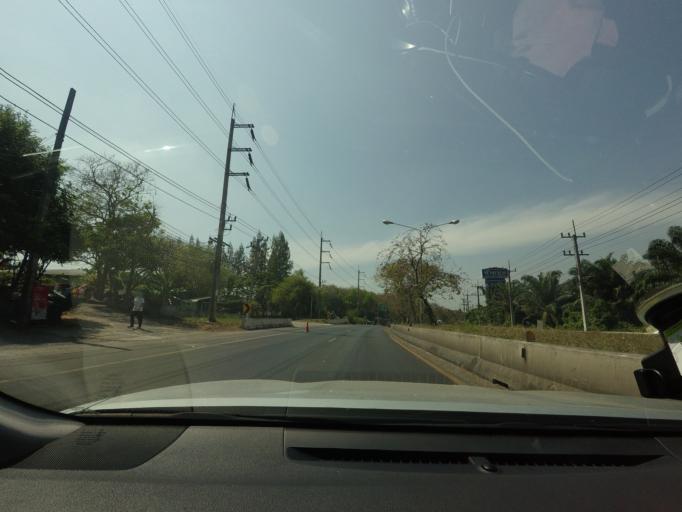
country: TH
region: Surat Thani
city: Kanchanadit
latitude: 9.1500
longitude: 99.4146
